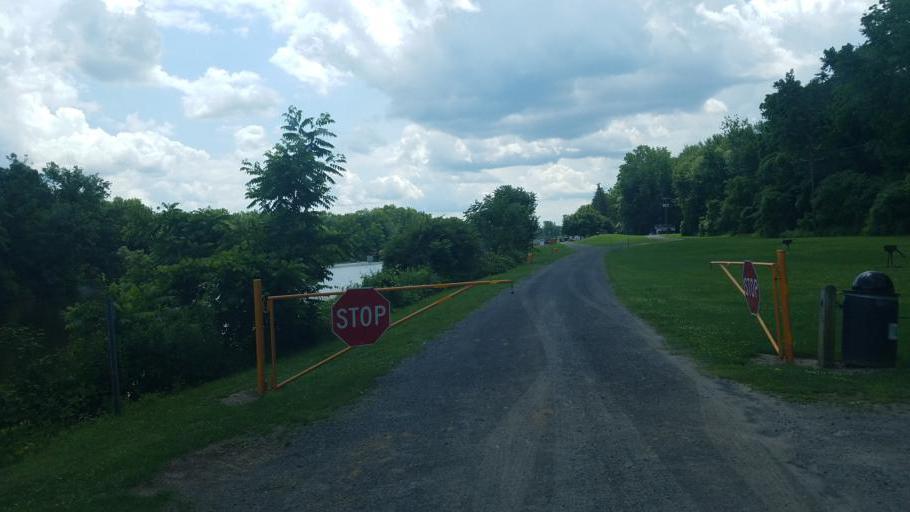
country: US
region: New York
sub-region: Wayne County
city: Clyde
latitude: 43.0613
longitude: -76.8397
